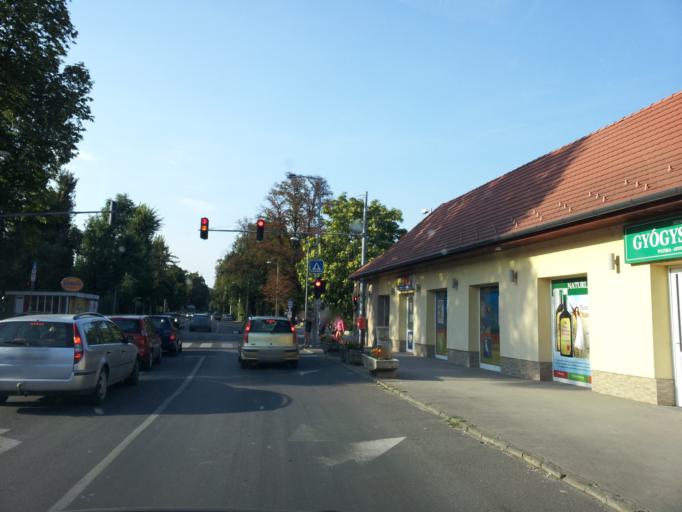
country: HU
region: Pest
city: Leanyfalu
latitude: 47.7185
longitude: 19.0894
